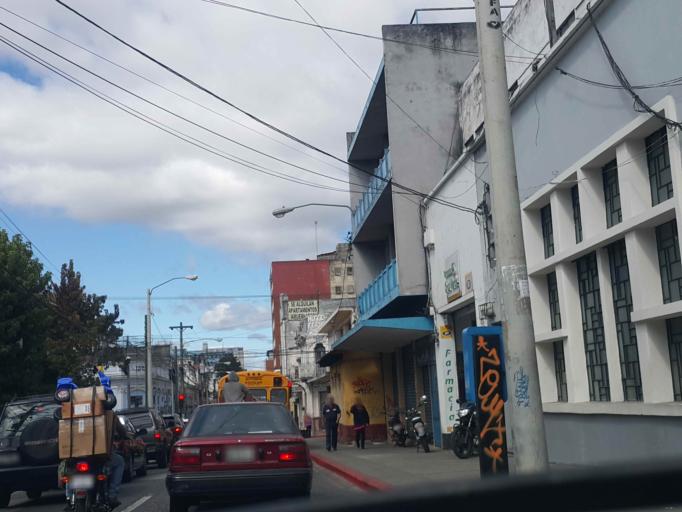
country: GT
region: Guatemala
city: Guatemala City
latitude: 14.6316
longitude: -90.5139
